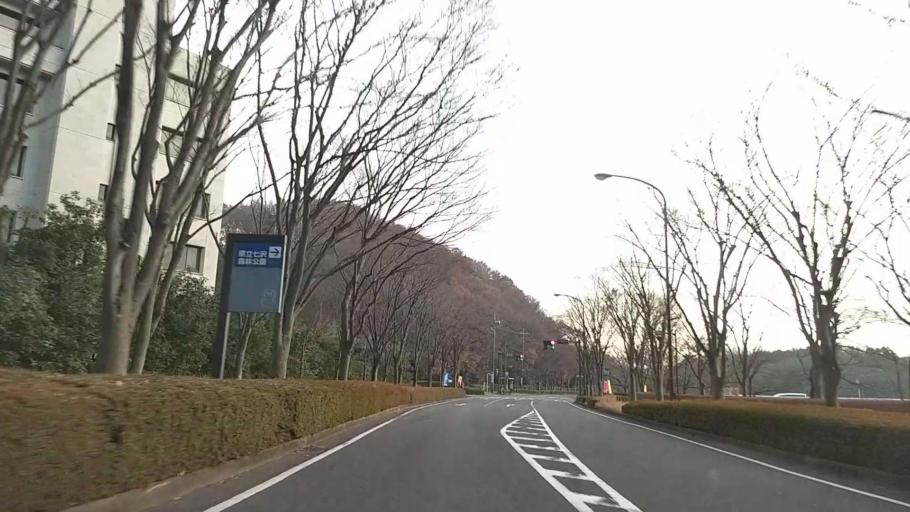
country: JP
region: Kanagawa
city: Atsugi
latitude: 35.4426
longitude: 139.3119
